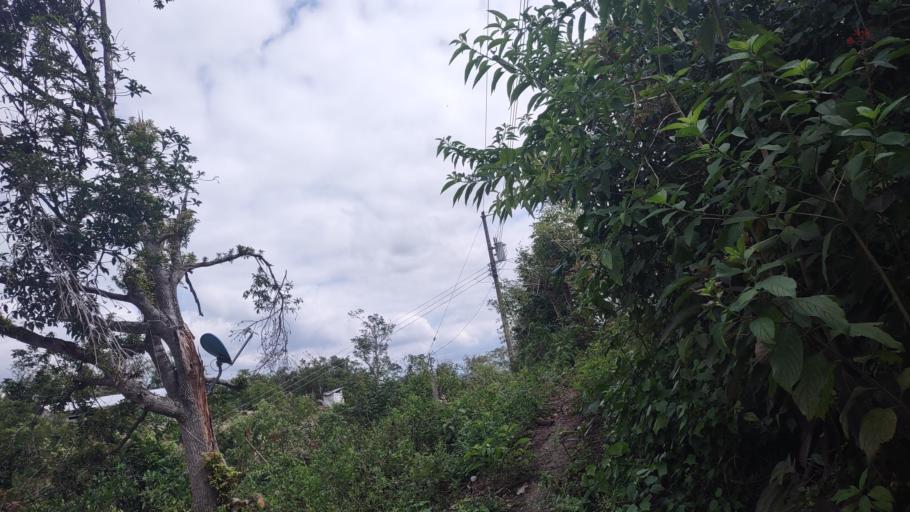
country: MX
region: Veracruz
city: Papantla de Olarte
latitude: 20.4678
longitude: -97.2743
